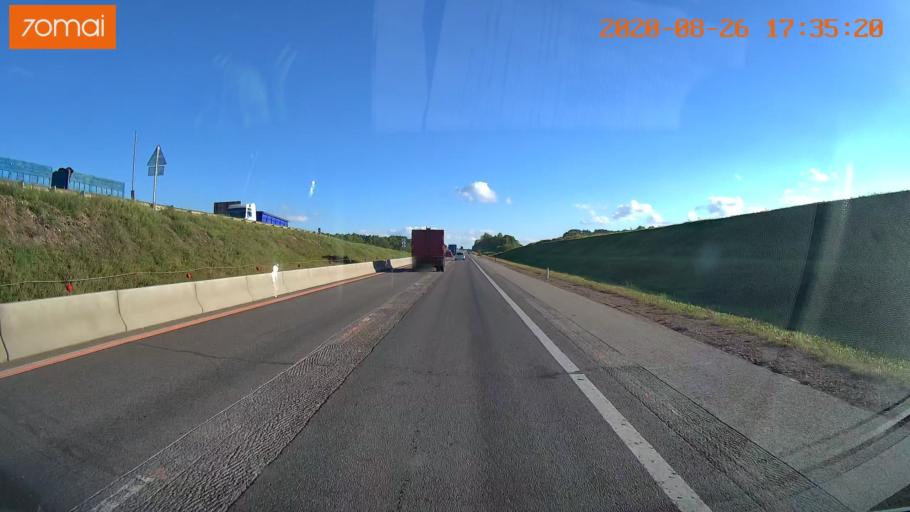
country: RU
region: Tula
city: Kazachka
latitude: 53.3849
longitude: 38.1844
